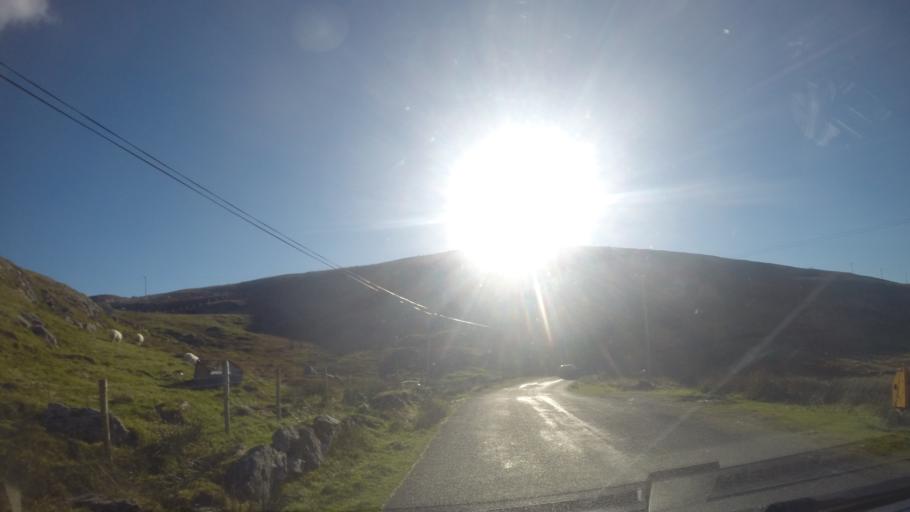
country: IE
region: Ulster
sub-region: County Donegal
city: Killybegs
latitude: 54.7060
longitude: -8.7573
